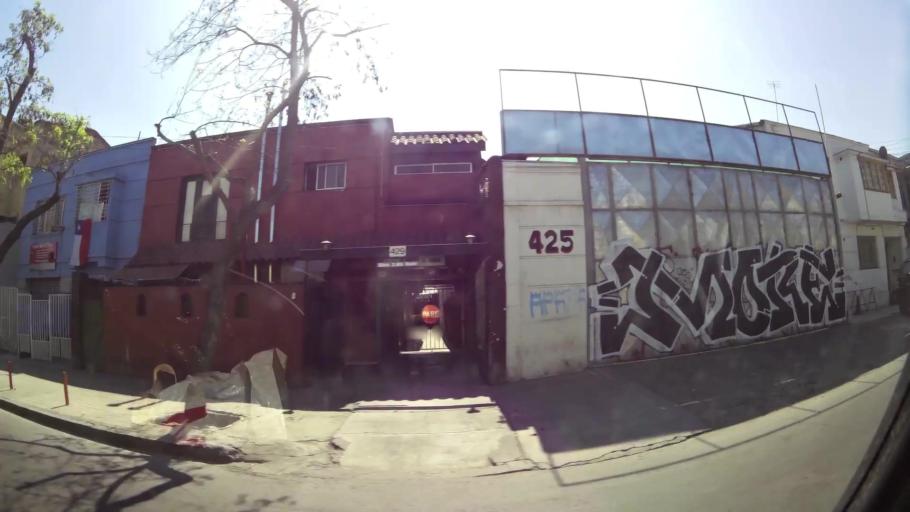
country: CL
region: Santiago Metropolitan
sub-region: Provincia de Santiago
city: Santiago
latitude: -33.4536
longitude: -70.6384
